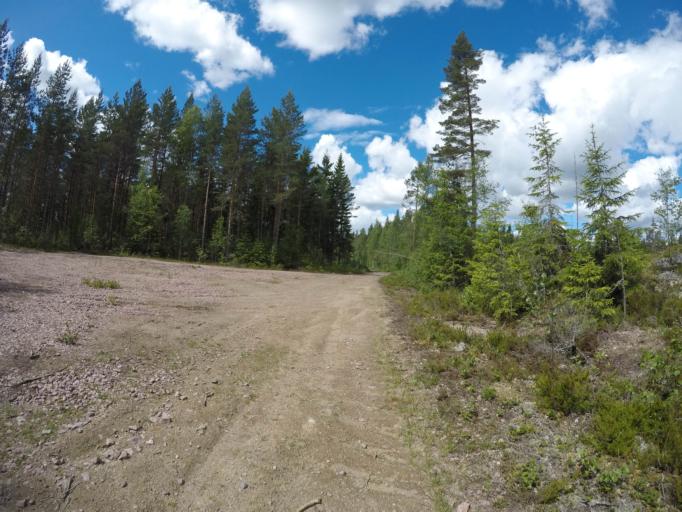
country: SE
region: Vaermland
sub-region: Filipstads Kommun
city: Lesjofors
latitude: 60.1360
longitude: 14.3098
